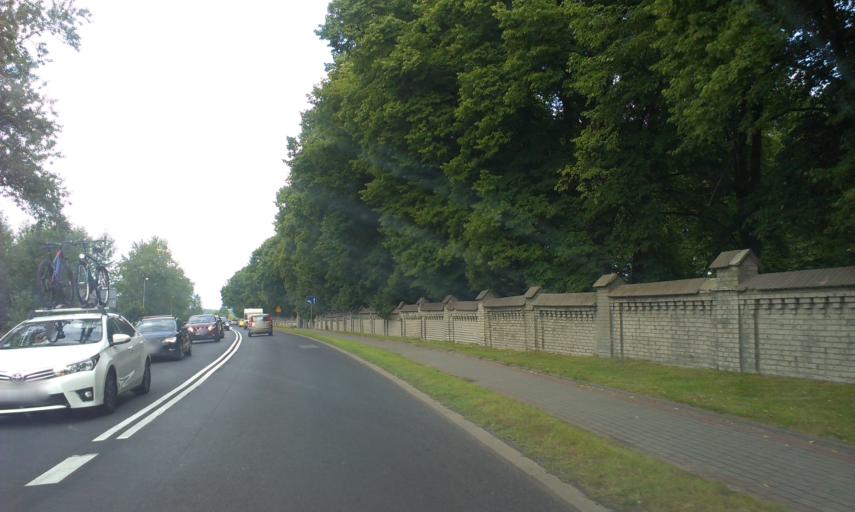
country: PL
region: West Pomeranian Voivodeship
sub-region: Powiat koszalinski
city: Bobolice
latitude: 53.9611
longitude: 16.5828
